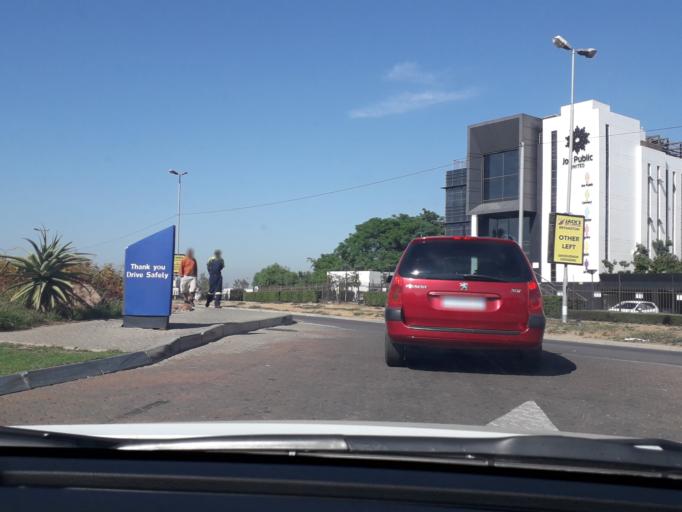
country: ZA
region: Gauteng
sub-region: City of Johannesburg Metropolitan Municipality
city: Diepsloot
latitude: -26.0544
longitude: 28.0238
